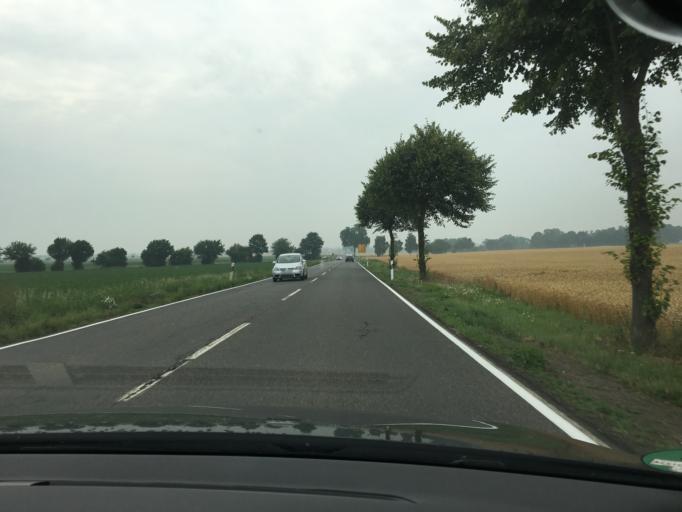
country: DE
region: North Rhine-Westphalia
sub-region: Regierungsbezirk Koln
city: Titz
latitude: 50.9891
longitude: 6.4086
